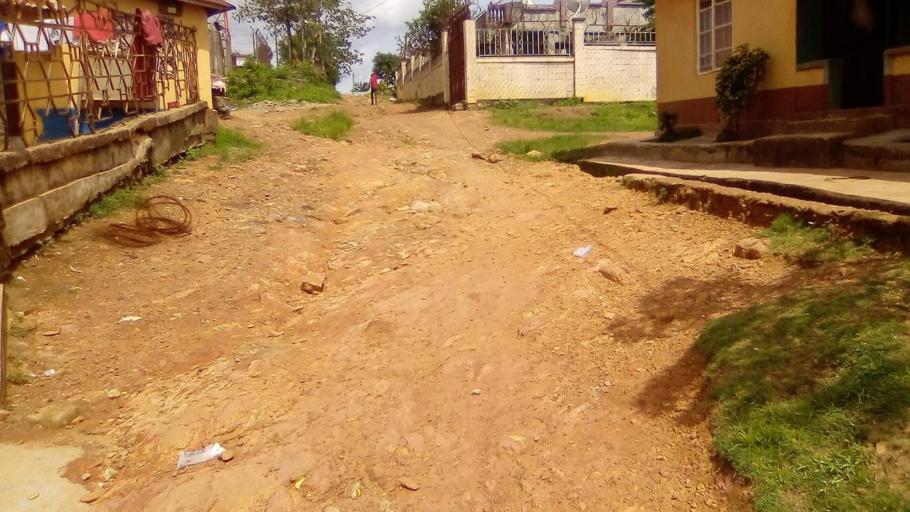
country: SL
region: Southern Province
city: Bo
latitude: 7.9679
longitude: -11.7307
